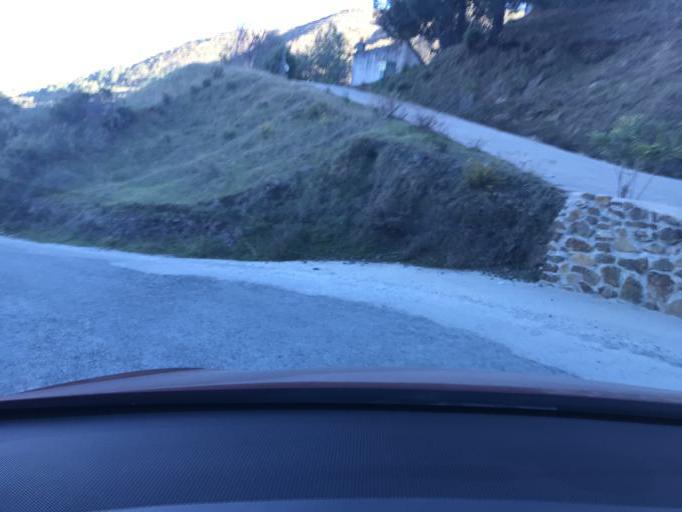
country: ES
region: Andalusia
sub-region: Provincia de Malaga
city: Tolox
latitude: 36.6813
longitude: -4.9102
